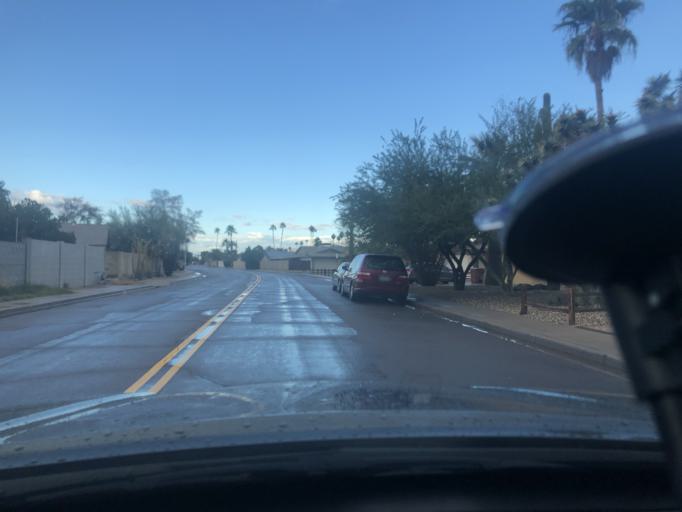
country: US
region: Arizona
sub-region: Maricopa County
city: Scottsdale
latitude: 33.4853
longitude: -111.8944
